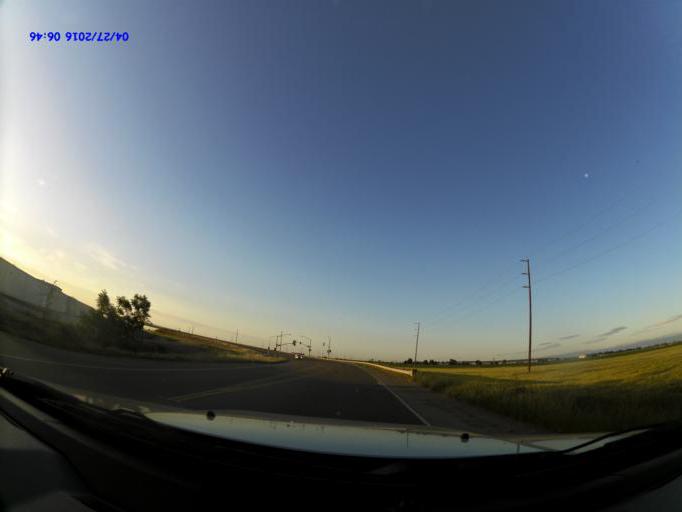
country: US
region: California
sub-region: San Joaquin County
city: Garden Acres
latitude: 37.9143
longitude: -121.1878
